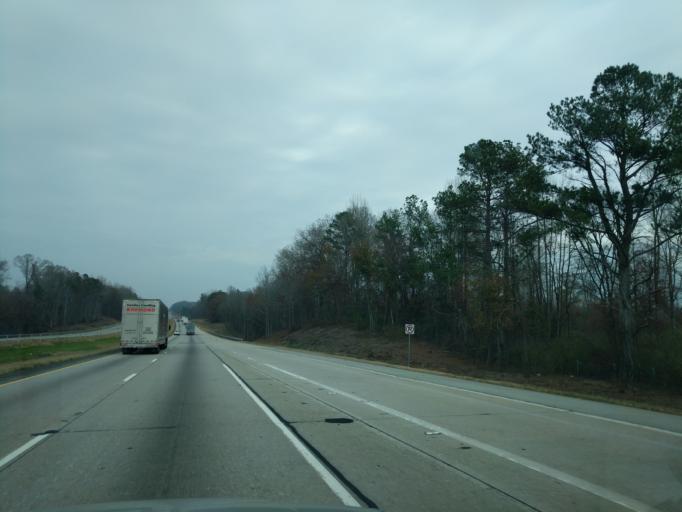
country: US
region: Georgia
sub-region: Banks County
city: Homer
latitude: 34.2989
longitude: -83.4045
